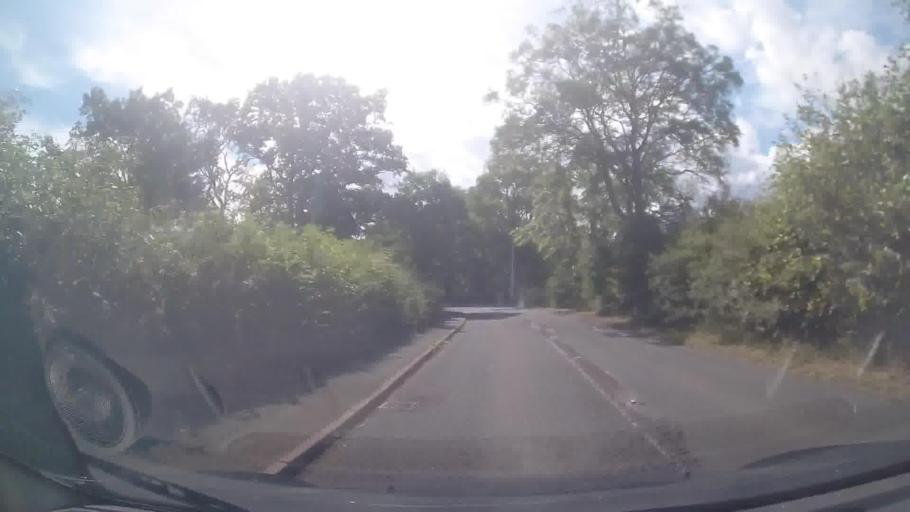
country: GB
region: Wales
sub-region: Sir Powys
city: Llandrindod Wells
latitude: 52.2137
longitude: -3.3930
